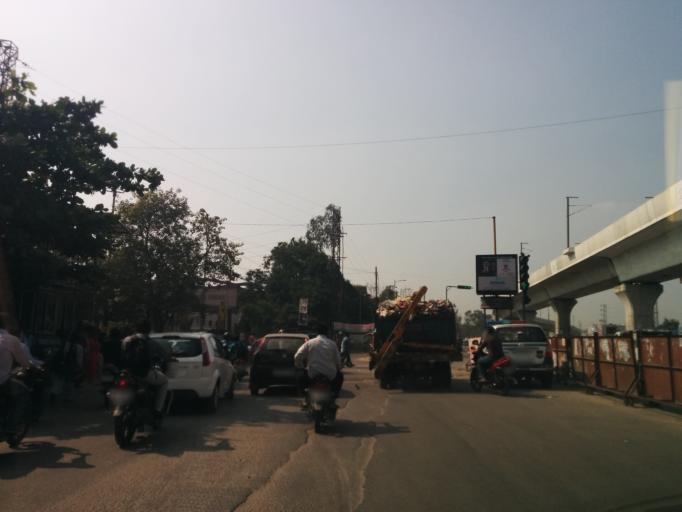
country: IN
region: Telangana
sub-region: Rangareddi
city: Kukatpalli
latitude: 17.4961
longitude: 78.3954
